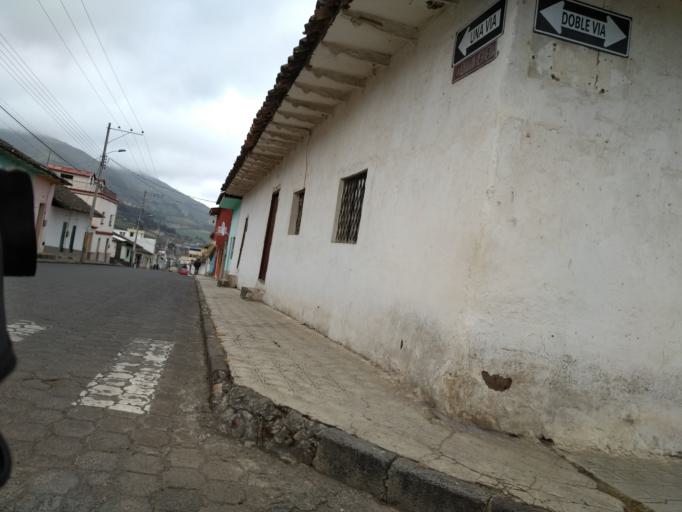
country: EC
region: Carchi
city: El Angel
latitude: 0.6249
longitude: -77.9380
